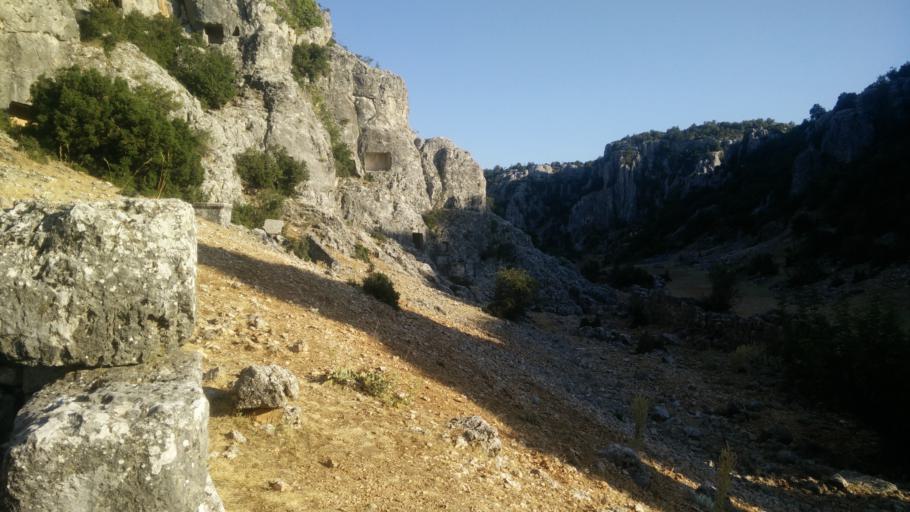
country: TR
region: Mersin
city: Kirobasi
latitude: 36.5860
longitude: 33.9691
